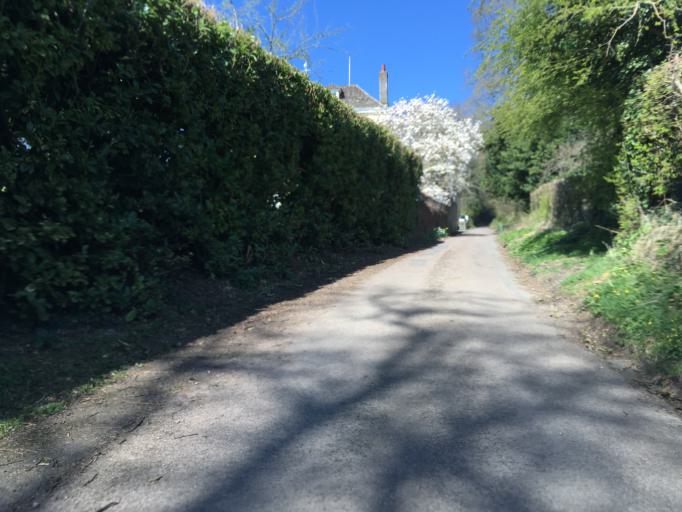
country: GB
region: England
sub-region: Gloucestershire
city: Wotton-under-Edge
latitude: 51.6409
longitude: -2.3490
